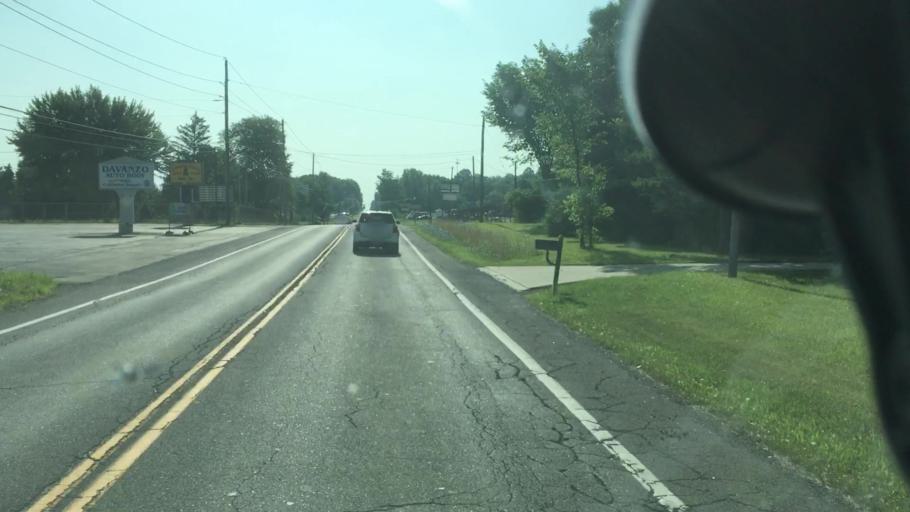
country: US
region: Ohio
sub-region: Mahoning County
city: Lowellville
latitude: 41.0238
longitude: -80.5737
